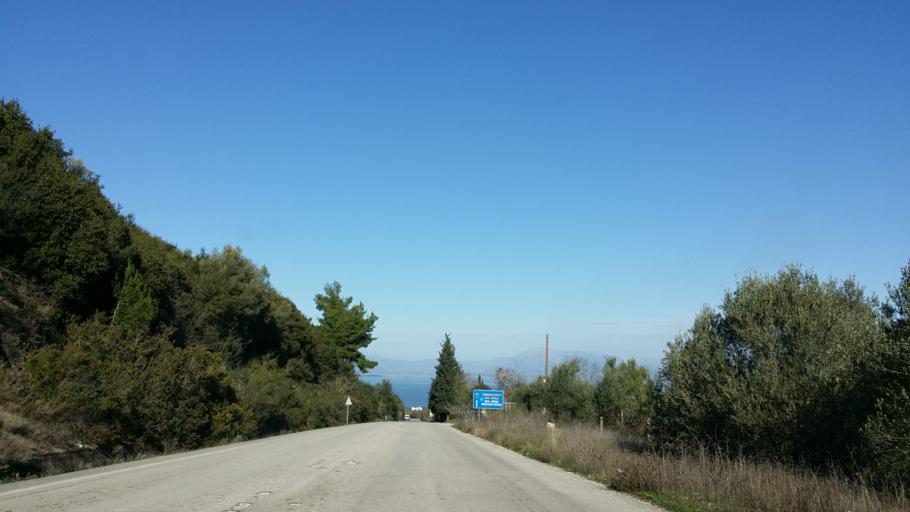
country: GR
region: West Greece
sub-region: Nomos Aitolias kai Akarnanias
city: Vonitsa
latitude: 38.9117
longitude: 20.9475
